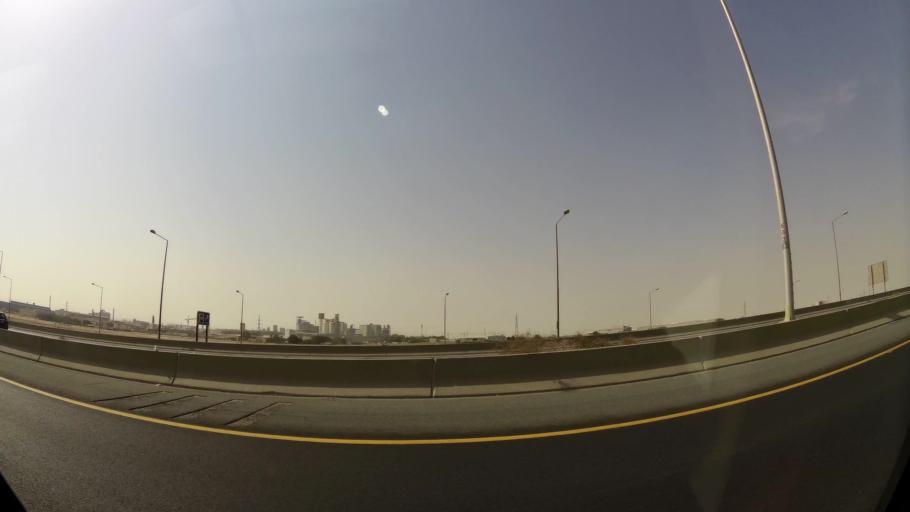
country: KW
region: Al Ahmadi
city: Al Fahahil
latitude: 29.0081
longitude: 48.1343
